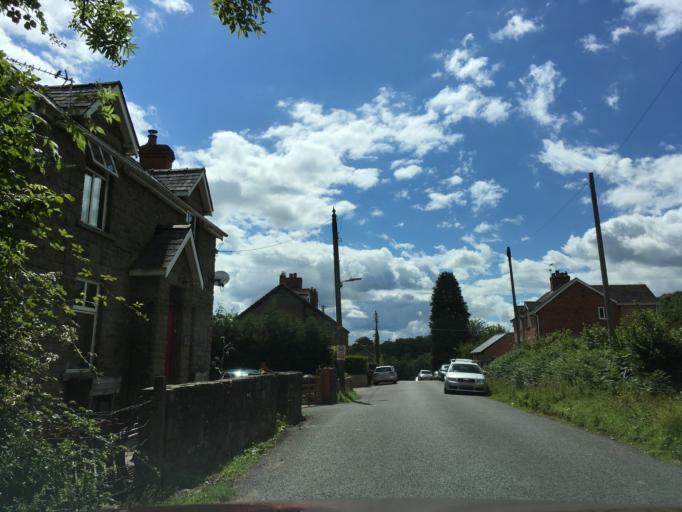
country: GB
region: England
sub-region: Gloucestershire
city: Bream
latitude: 51.7454
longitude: -2.5597
